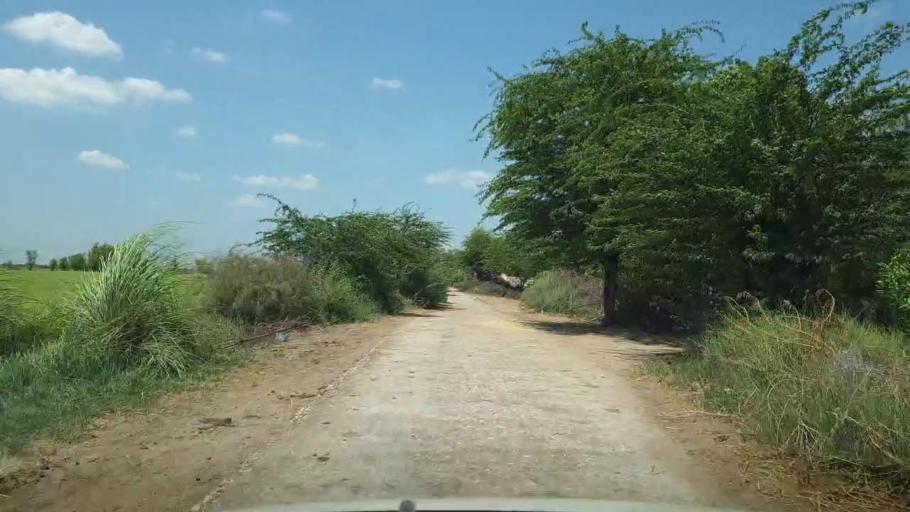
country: PK
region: Sindh
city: Sanghar
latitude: 26.0695
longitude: 69.0478
